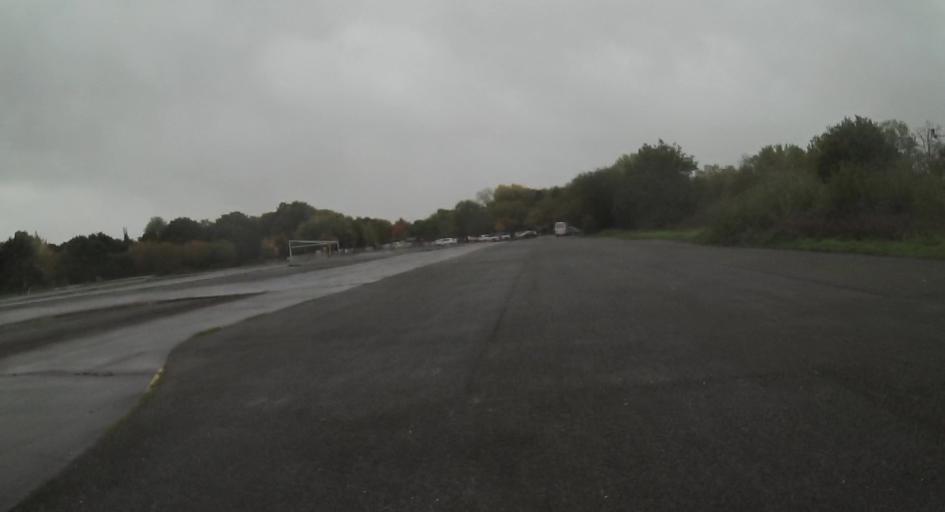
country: GB
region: England
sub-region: Surrey
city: Byfleet
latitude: 51.3452
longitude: -0.4716
